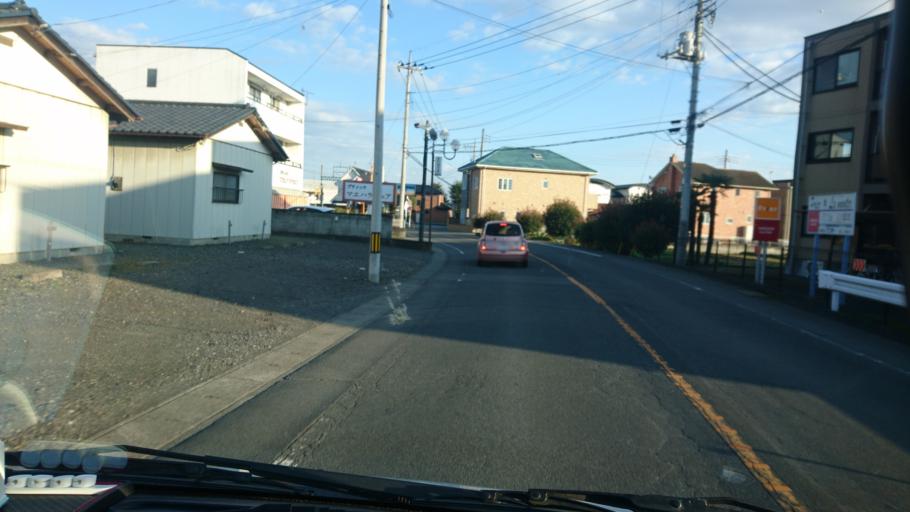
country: JP
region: Gunma
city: Omamacho-omama
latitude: 36.4184
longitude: 139.2986
